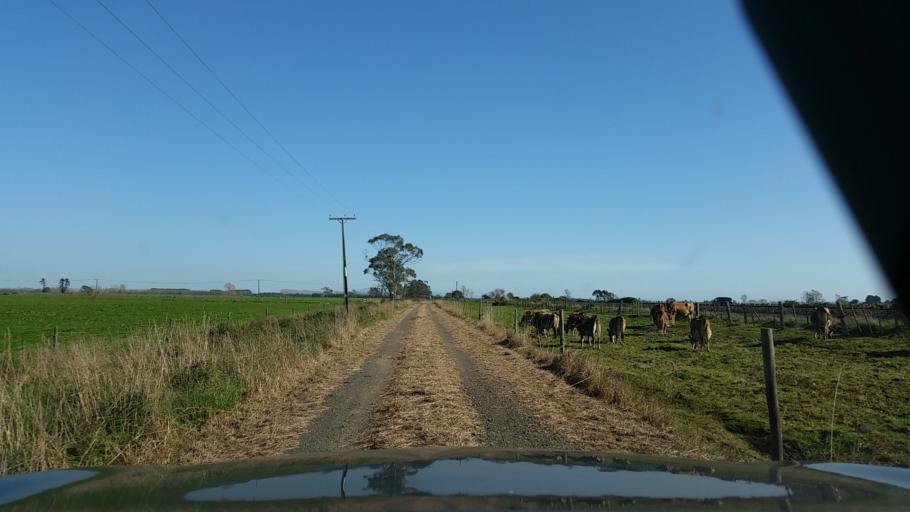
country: NZ
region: Waikato
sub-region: Waipa District
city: Cambridge
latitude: -37.6834
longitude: 175.4542
